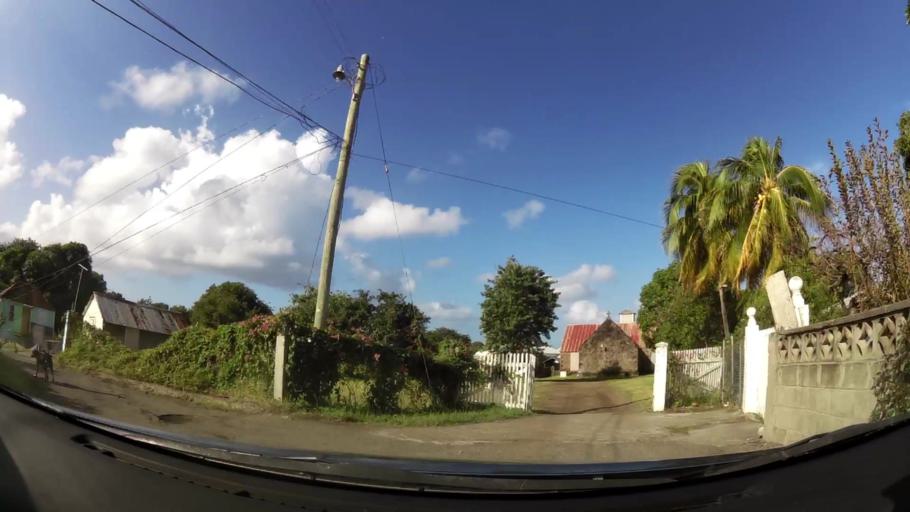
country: KN
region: Saint Paul Charlestown
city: Charlestown
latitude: 17.1416
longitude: -62.6281
